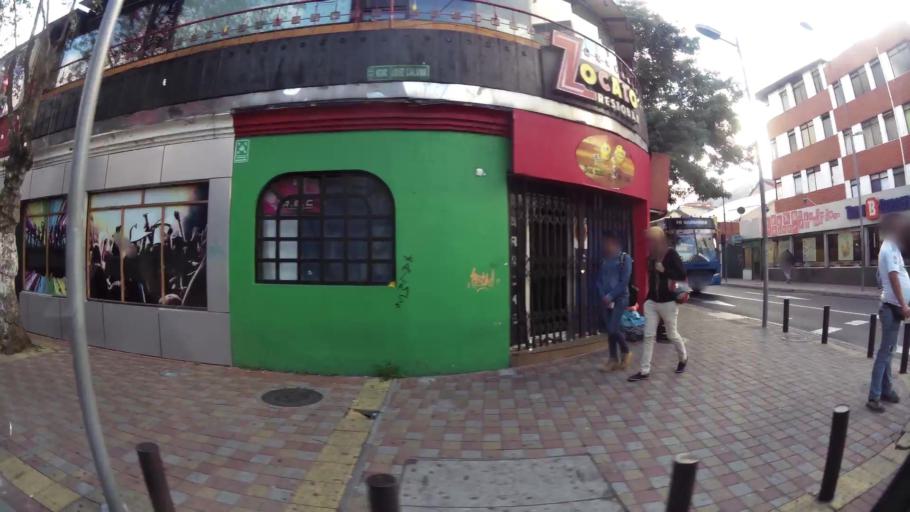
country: EC
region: Pichincha
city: Quito
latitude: -0.2019
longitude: -78.4911
